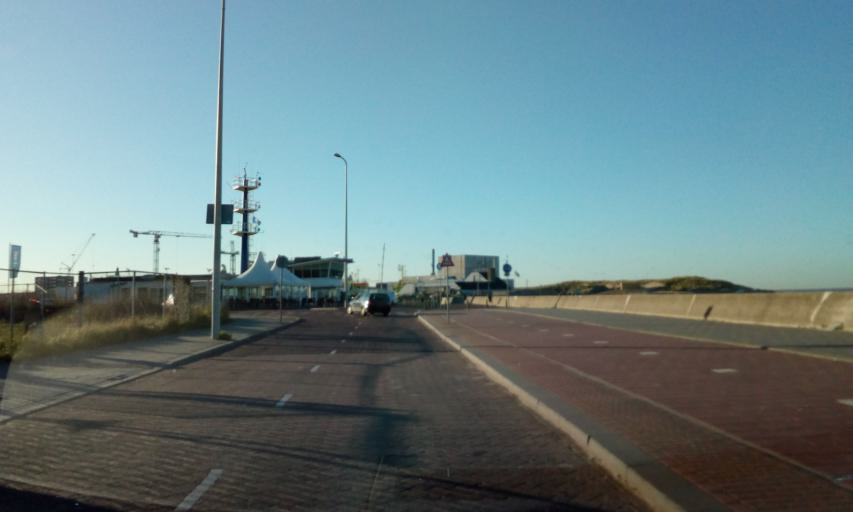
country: NL
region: South Holland
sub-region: Gemeente Den Haag
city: Scheveningen
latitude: 52.1002
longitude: 4.2619
